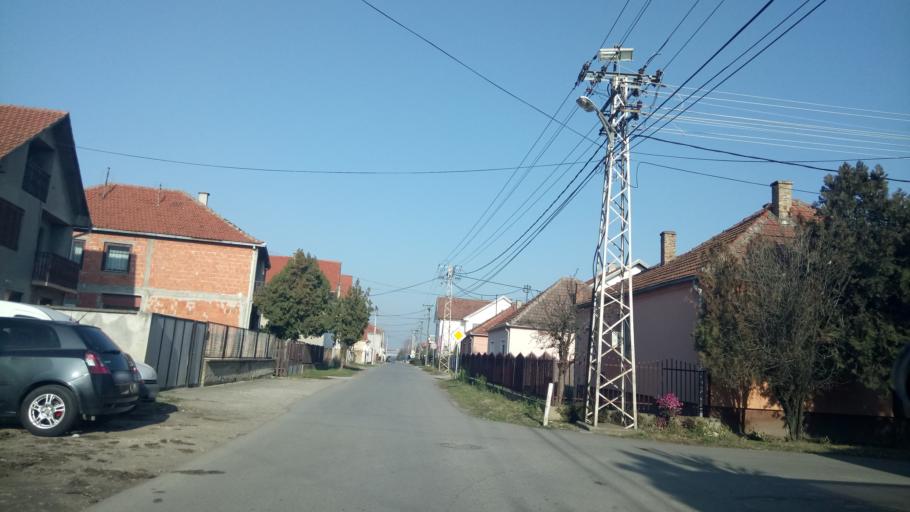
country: RS
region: Autonomna Pokrajina Vojvodina
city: Nova Pazova
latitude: 44.9459
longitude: 20.2045
